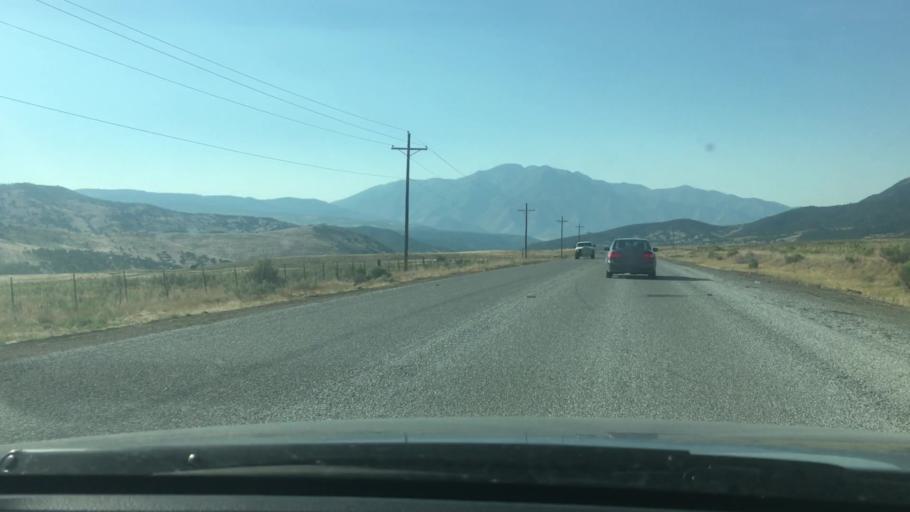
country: US
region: Utah
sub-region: Utah County
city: Woodland Hills
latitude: 39.8443
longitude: -111.5155
